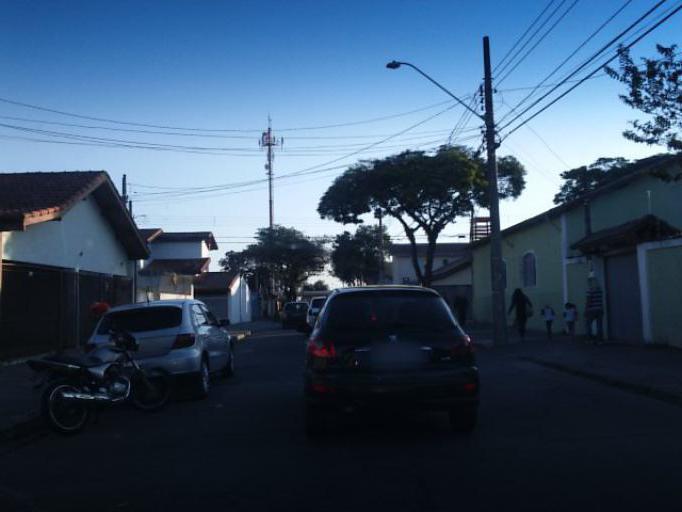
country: BR
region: Sao Paulo
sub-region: Sao Jose Dos Campos
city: Sao Jose dos Campos
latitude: -23.1632
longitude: -45.8932
